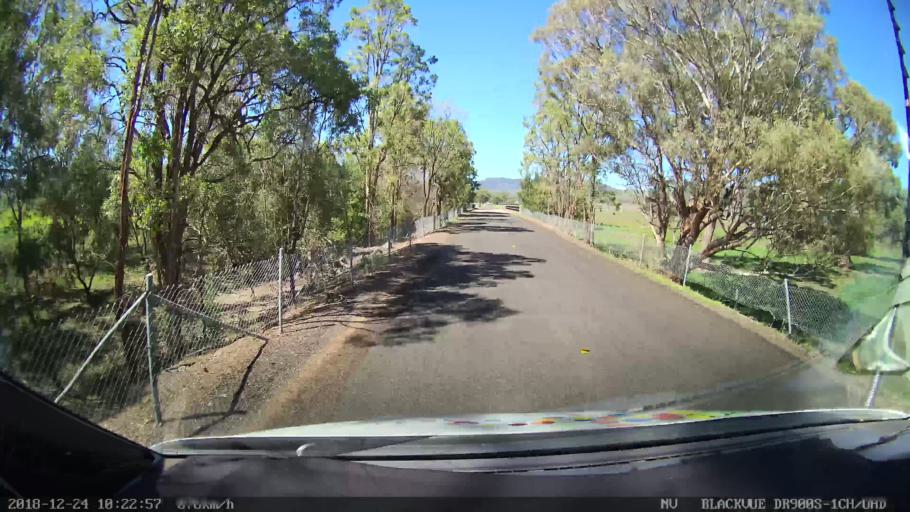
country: AU
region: New South Wales
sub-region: Liverpool Plains
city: Quirindi
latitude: -31.7701
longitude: 150.5413
